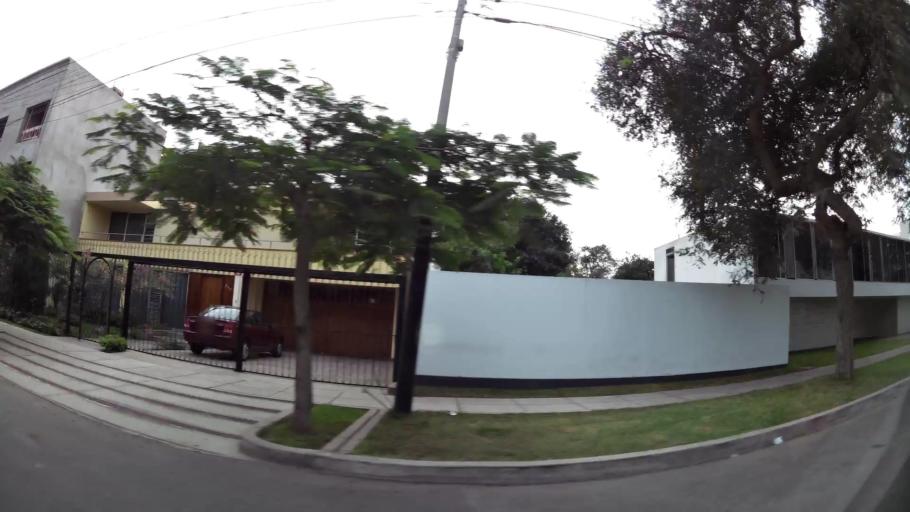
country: PE
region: Lima
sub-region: Lima
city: San Isidro
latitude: -12.1059
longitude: -77.0512
